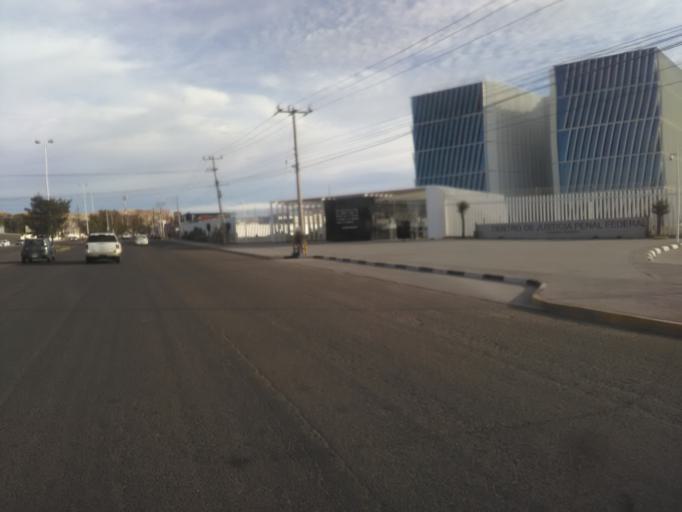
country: MX
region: Durango
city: Victoria de Durango
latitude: 24.0435
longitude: -104.6581
